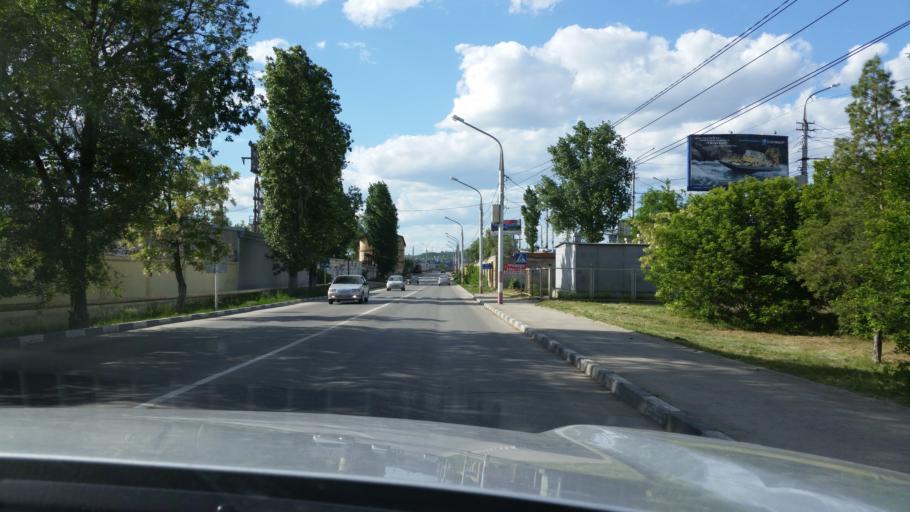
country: RU
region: Saratov
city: Engel's
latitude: 51.5034
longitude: 46.0792
